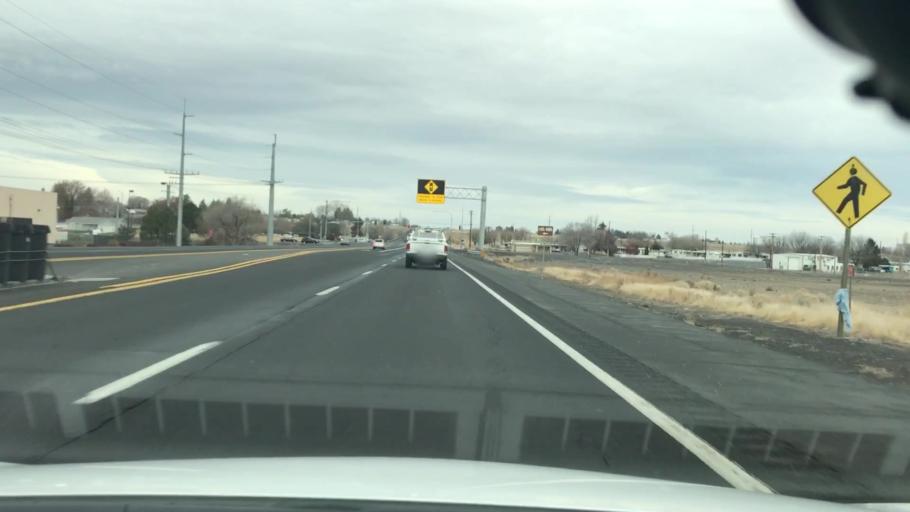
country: US
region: Washington
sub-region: Grant County
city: Moses Lake
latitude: 47.1485
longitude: -119.2911
